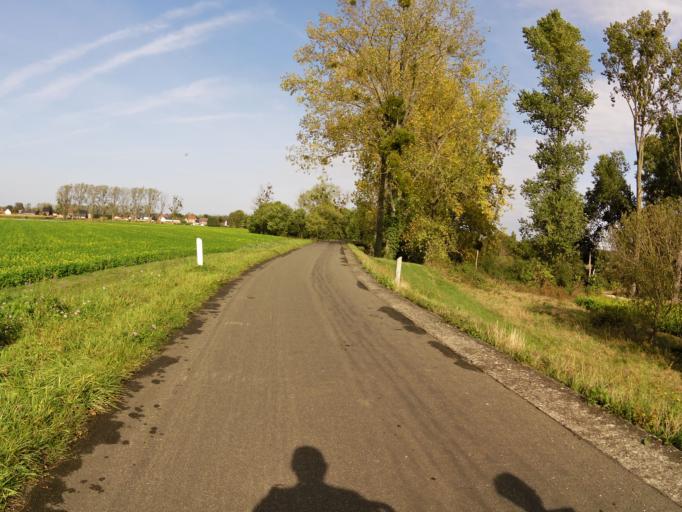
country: NL
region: Limburg
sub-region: Gemeente Stein
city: Elsloo
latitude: 50.9420
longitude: 5.7412
